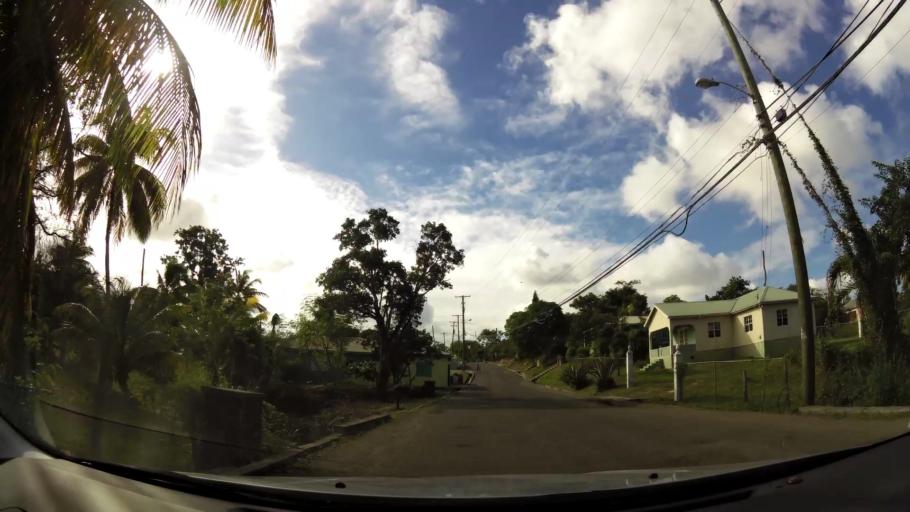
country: AG
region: Saint Peter
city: All Saints
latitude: 17.0507
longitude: -61.7974
